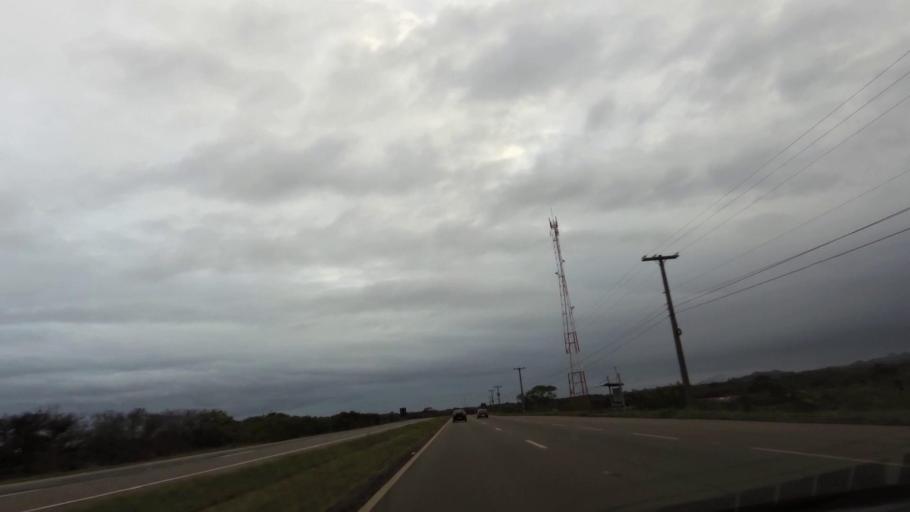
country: BR
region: Espirito Santo
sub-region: Guarapari
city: Guarapari
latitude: -20.5773
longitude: -40.4155
